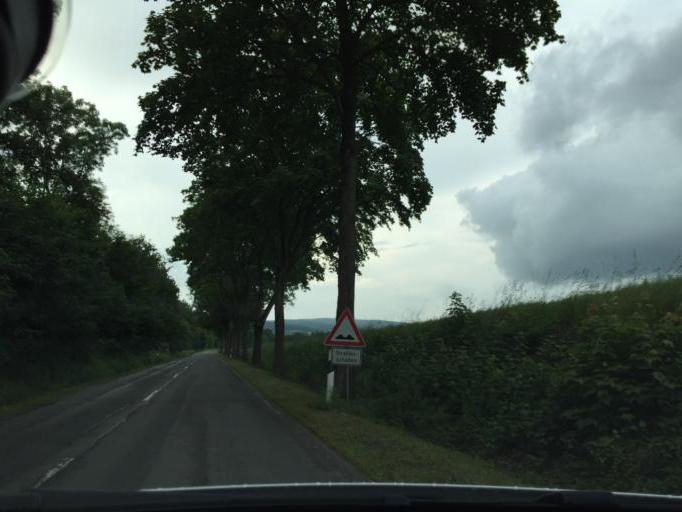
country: DE
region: Lower Saxony
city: Ottenstein
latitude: 51.9971
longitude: 9.3637
